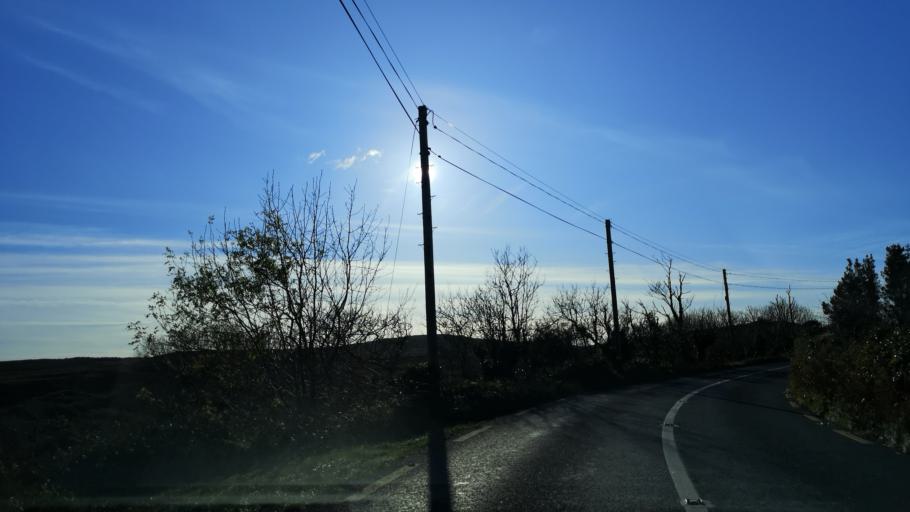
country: IE
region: Connaught
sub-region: County Galway
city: Clifden
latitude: 53.5410
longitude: -10.0081
